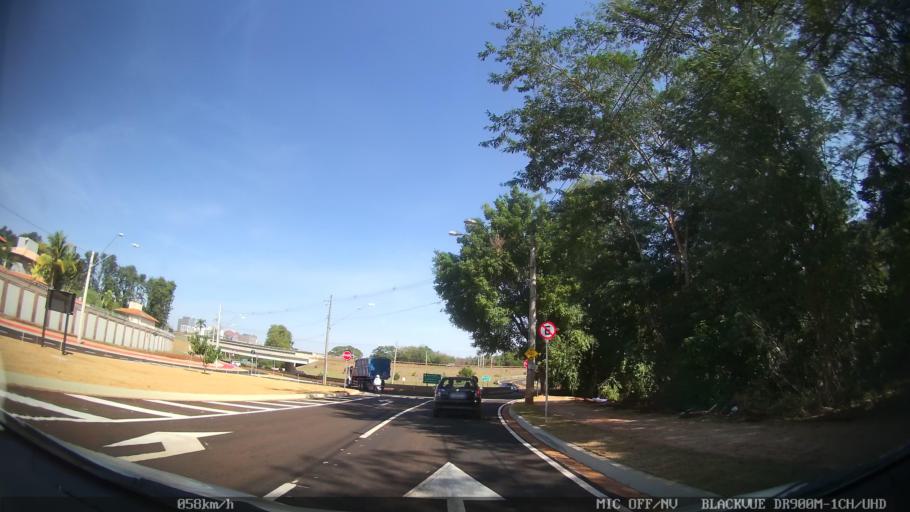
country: BR
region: Sao Paulo
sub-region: Ribeirao Preto
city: Ribeirao Preto
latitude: -21.2146
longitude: -47.8354
